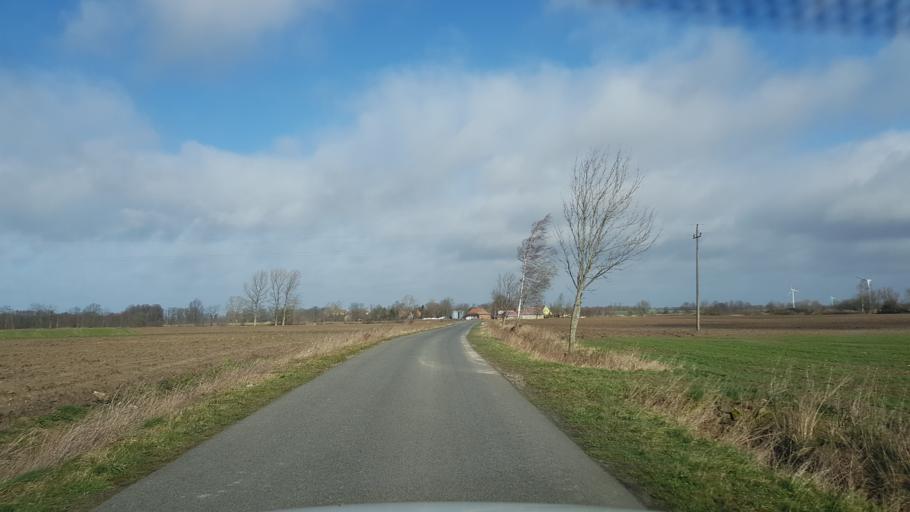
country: PL
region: West Pomeranian Voivodeship
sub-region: Powiat slawienski
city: Slawno
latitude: 54.5056
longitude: 16.6521
